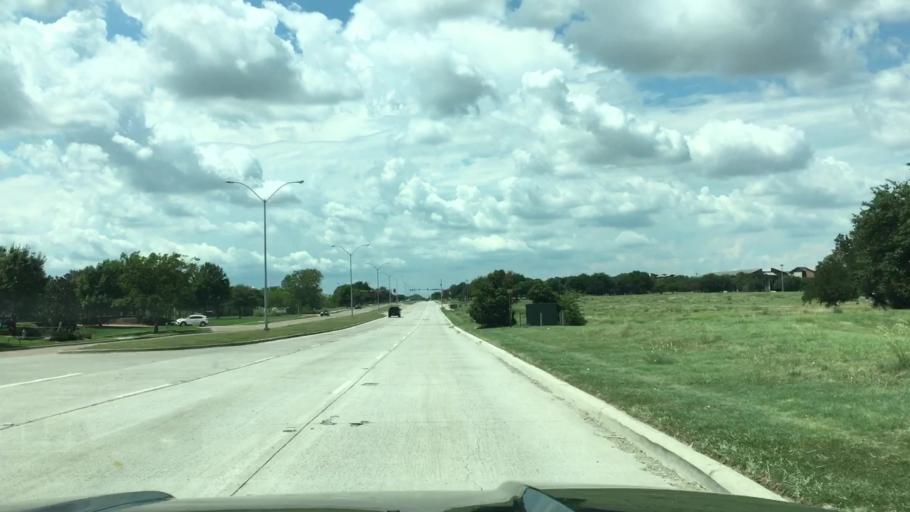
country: US
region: Texas
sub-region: Tarrant County
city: Blue Mound
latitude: 32.8613
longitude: -97.3204
